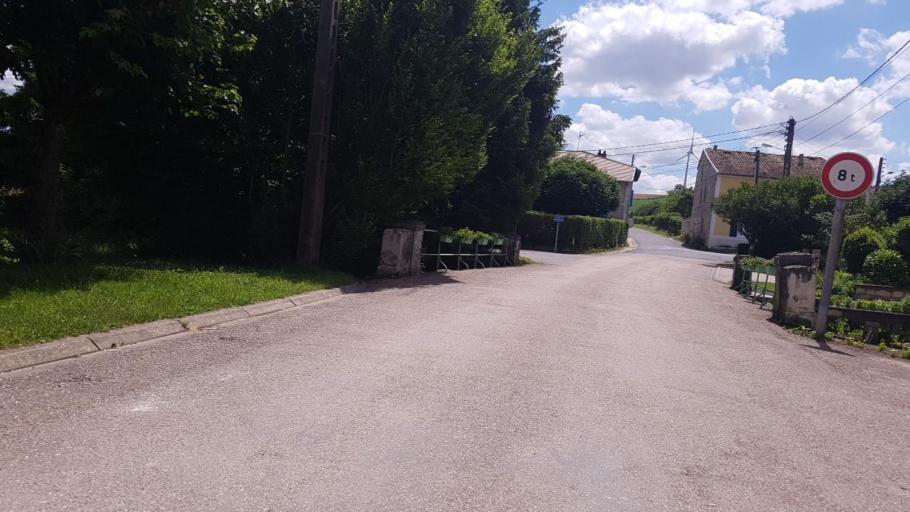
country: FR
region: Lorraine
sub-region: Departement de la Meuse
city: Vacon
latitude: 48.6454
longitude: 5.5138
